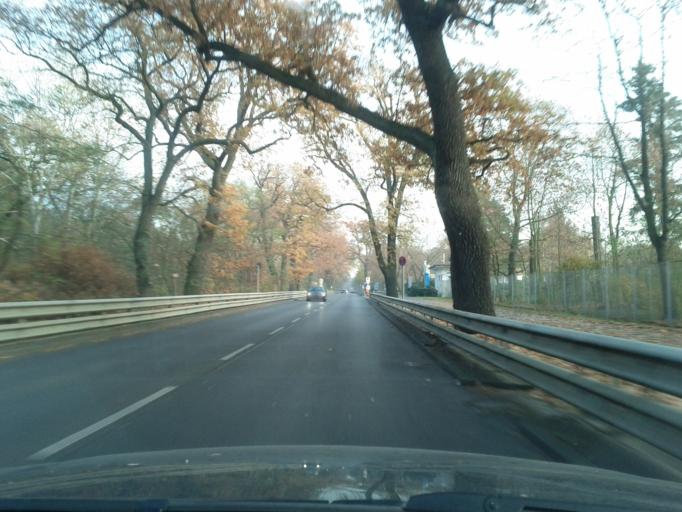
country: DE
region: Berlin
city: Rahnsdorf
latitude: 52.4460
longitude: 13.6753
